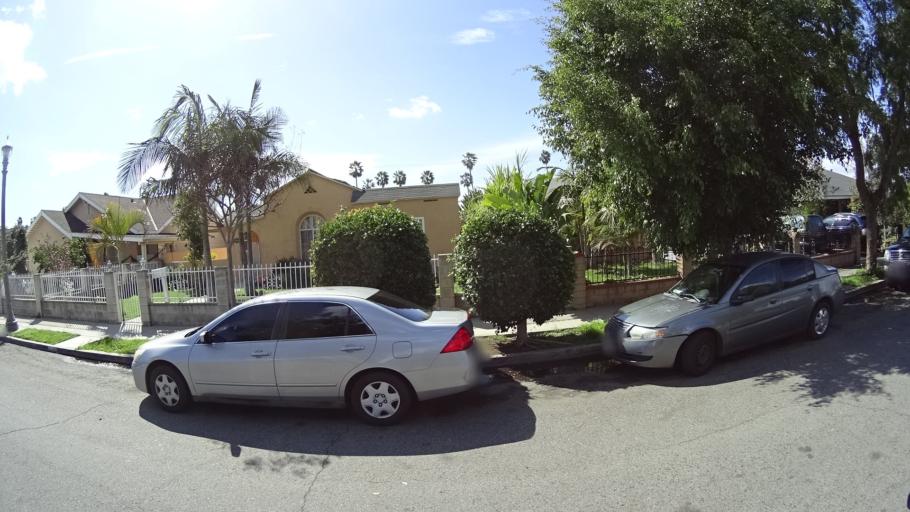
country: US
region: California
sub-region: Orange County
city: Anaheim
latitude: 33.8441
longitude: -117.9154
